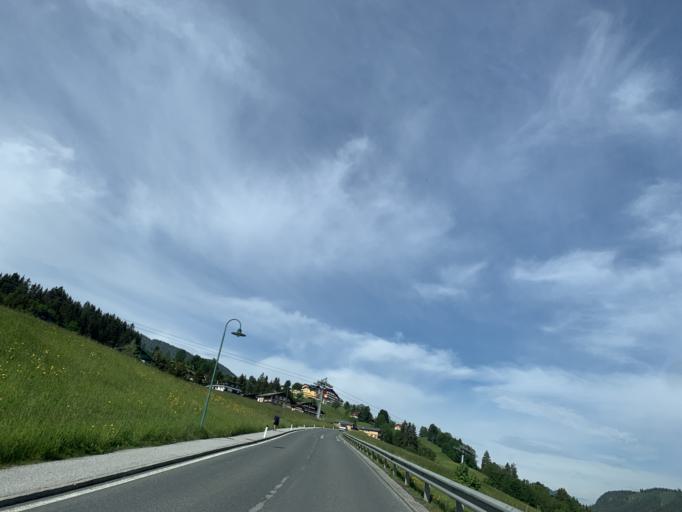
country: AT
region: Styria
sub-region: Politischer Bezirk Liezen
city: Schladming
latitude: 47.3888
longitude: 13.6832
